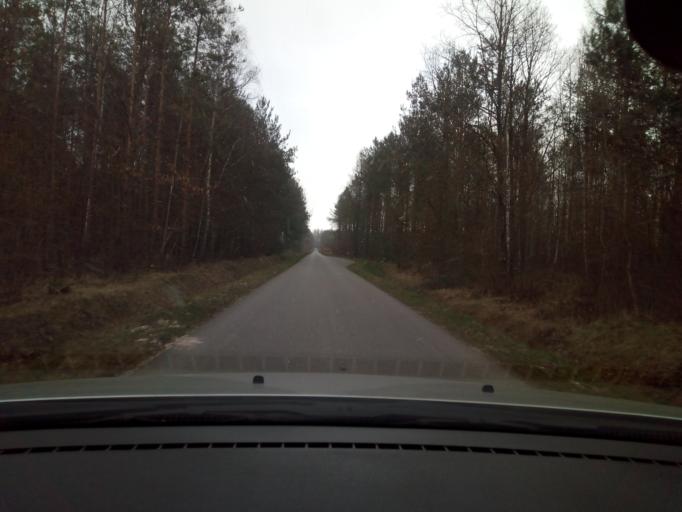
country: PL
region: Masovian Voivodeship
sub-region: Powiat lipski
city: Rzeczniow
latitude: 51.0793
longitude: 21.3368
